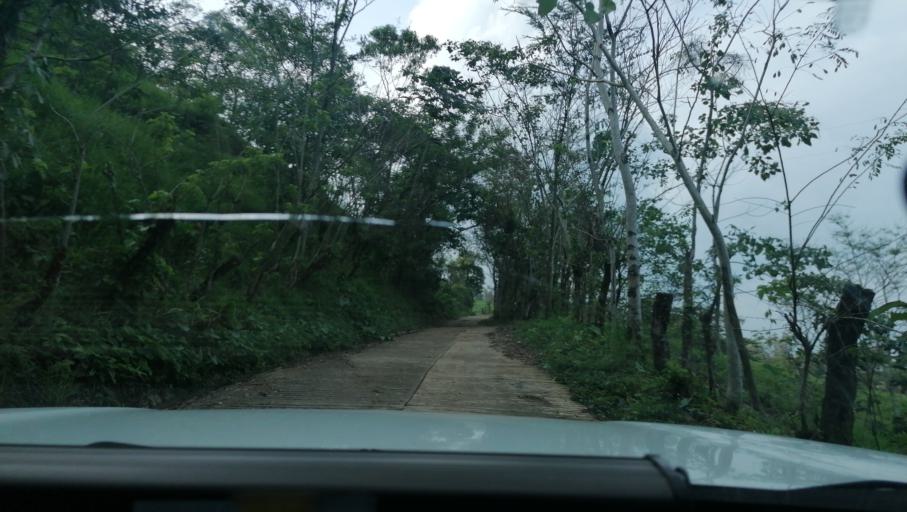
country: MX
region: Chiapas
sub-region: Tapilula
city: San Francisco Jacona
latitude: 17.3317
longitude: -93.1032
